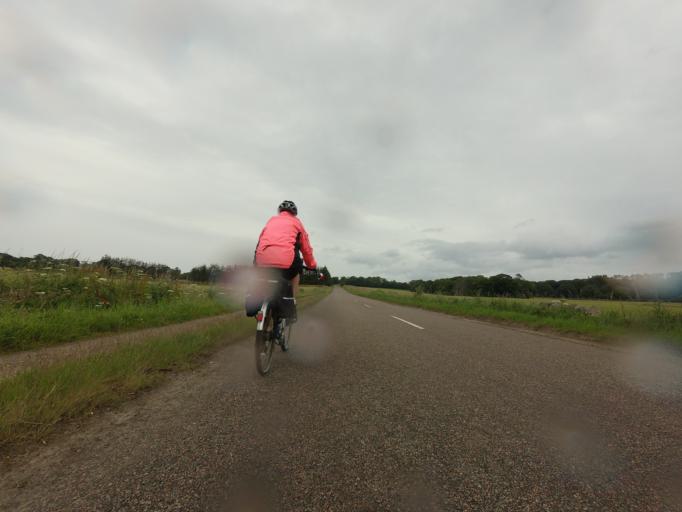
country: GB
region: Scotland
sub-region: Moray
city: Cullen
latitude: 57.6784
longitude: -2.8131
